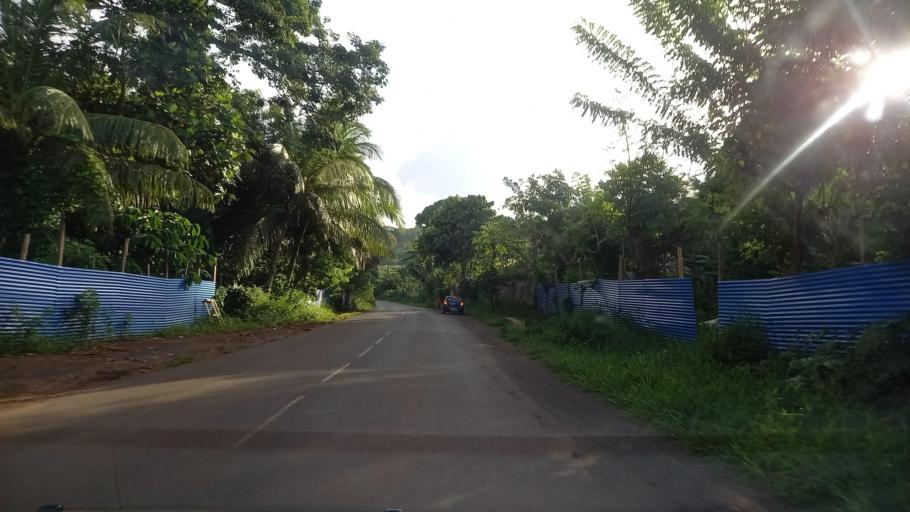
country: YT
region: Bandraboua
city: Bandraboua
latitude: -12.7274
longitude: 45.1210
